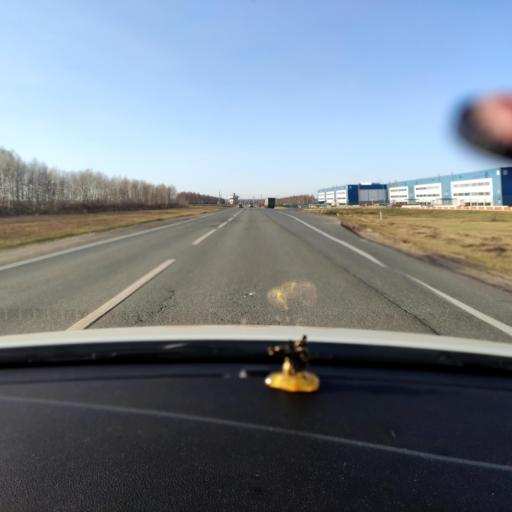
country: RU
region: Tatarstan
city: Stolbishchi
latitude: 55.6329
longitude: 49.2581
